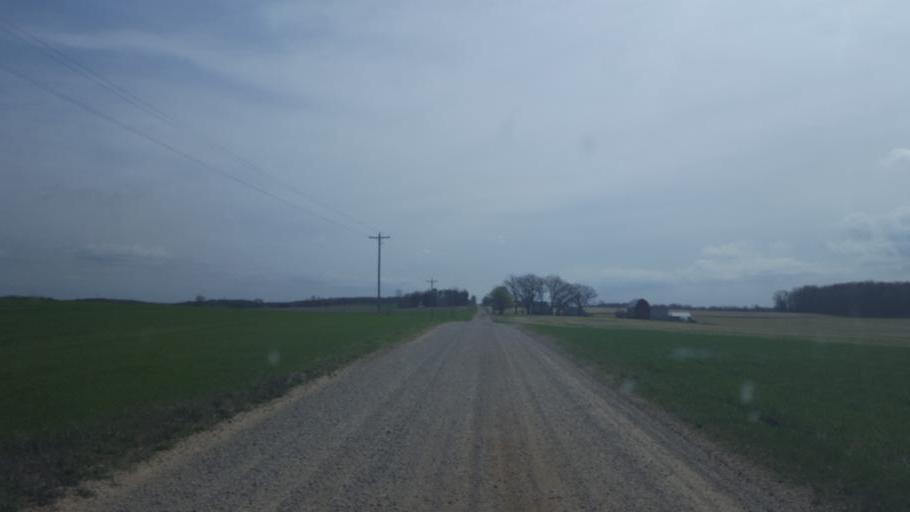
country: US
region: Michigan
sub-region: Montcalm County
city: Edmore
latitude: 43.4441
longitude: -84.9915
